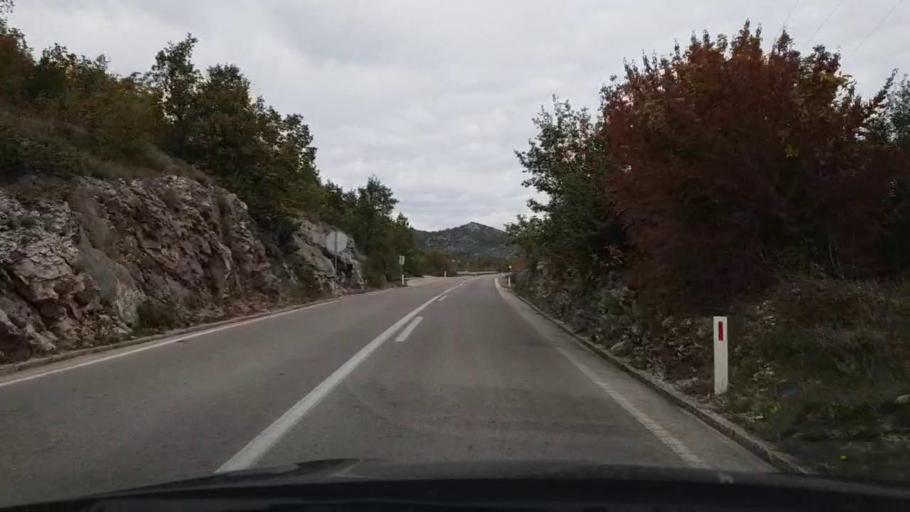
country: HR
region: Dubrovacko-Neretvanska
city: Cibaca
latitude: 42.6626
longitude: 18.2109
